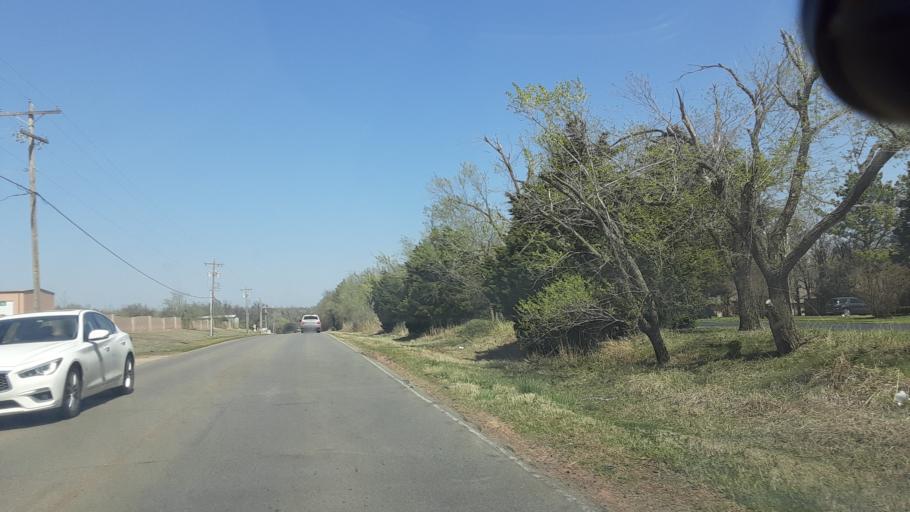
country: US
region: Oklahoma
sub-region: Oklahoma County
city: Edmond
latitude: 35.7331
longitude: -97.4784
